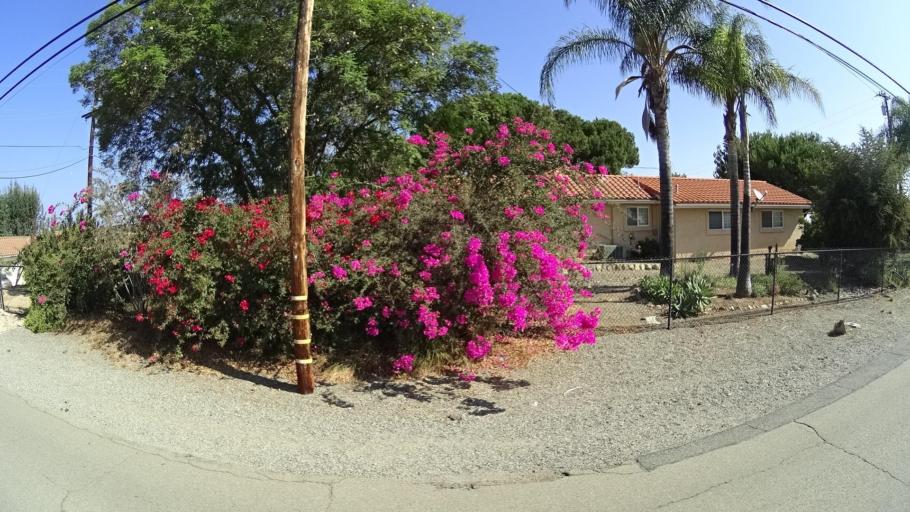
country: US
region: California
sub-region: San Diego County
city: Fallbrook
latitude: 33.3912
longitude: -117.2332
